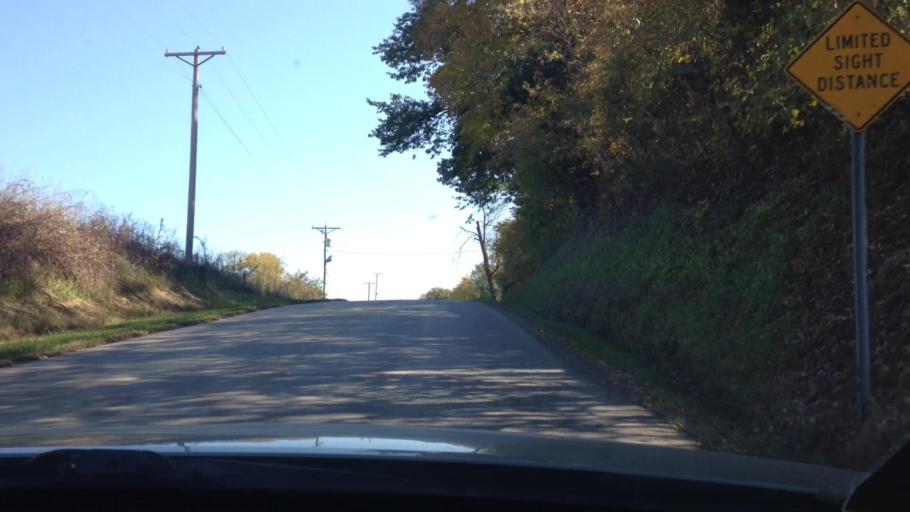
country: US
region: Missouri
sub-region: Platte County
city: Platte City
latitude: 39.3318
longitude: -94.8470
